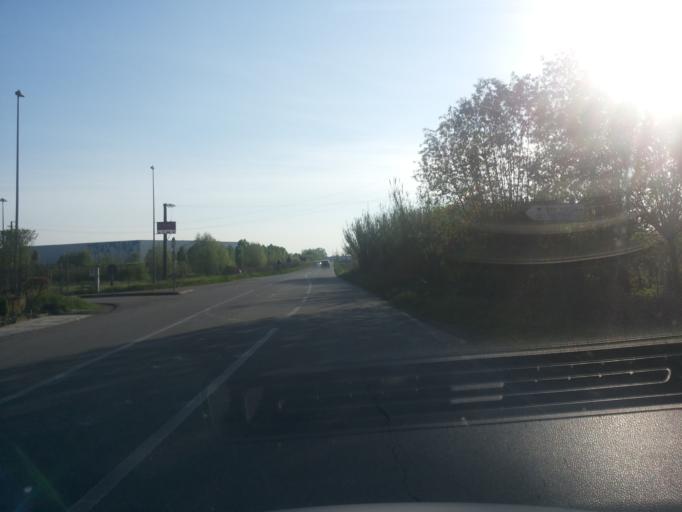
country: IT
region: Lombardy
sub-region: Provincia di Pavia
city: Mortara
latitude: 45.2475
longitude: 8.7114
